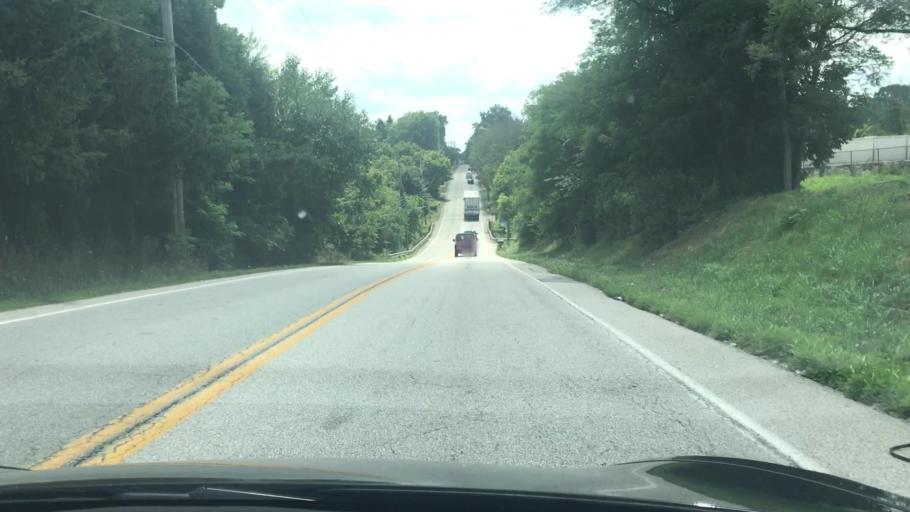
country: US
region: Pennsylvania
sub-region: York County
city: Manchester
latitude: 40.0761
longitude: -76.7654
